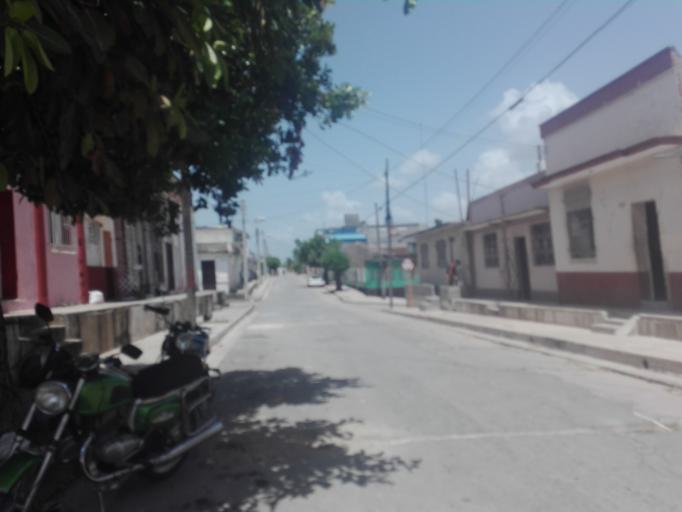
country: CU
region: Cienfuegos
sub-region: Municipio de Cienfuegos
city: Cienfuegos
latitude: 22.1483
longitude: -80.4380
